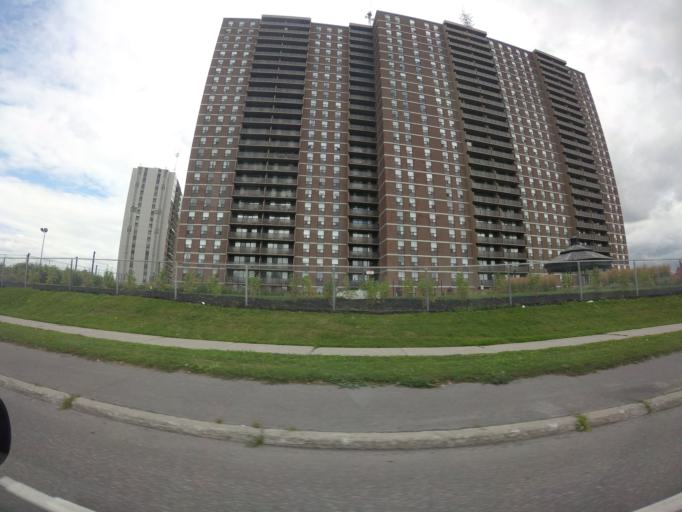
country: CA
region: Ontario
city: Ottawa
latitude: 45.4471
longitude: -75.6237
